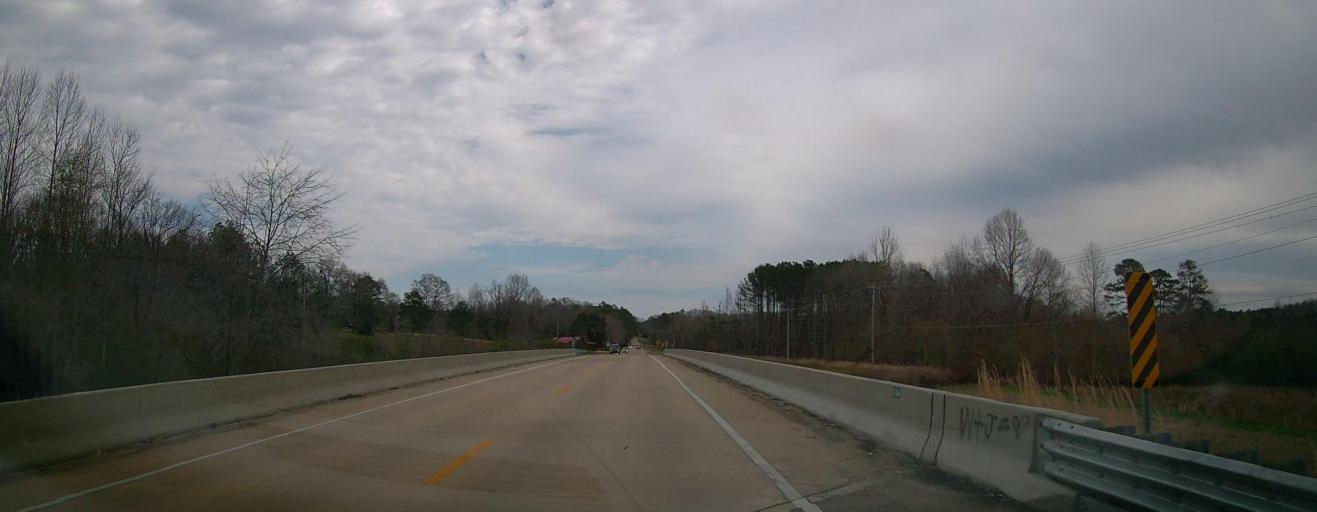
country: US
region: Mississippi
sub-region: Itawamba County
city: Fulton
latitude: 34.2531
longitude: -88.3076
